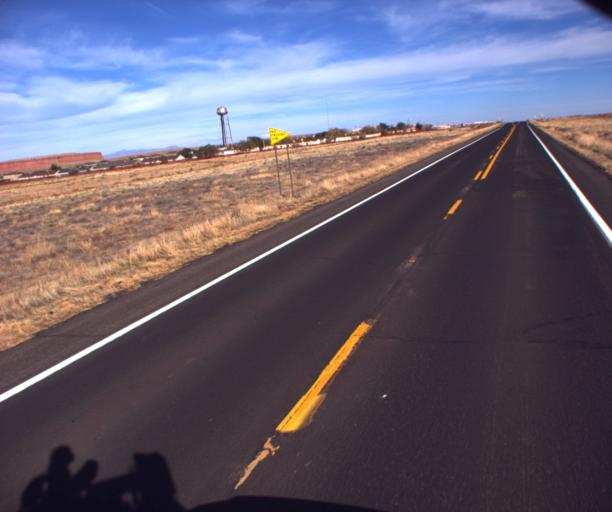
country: US
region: Arizona
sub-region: Apache County
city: Lukachukai
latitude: 36.9610
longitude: -109.3881
